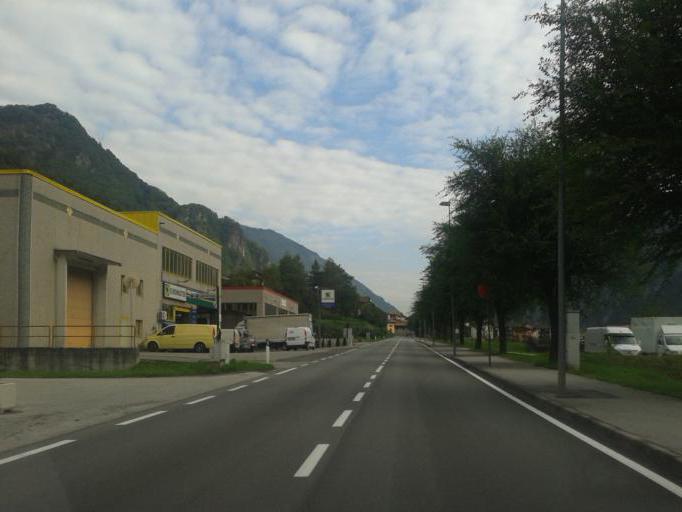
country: IT
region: Trentino-Alto Adige
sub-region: Provincia di Trento
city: Condino
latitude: 45.8814
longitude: 10.5934
